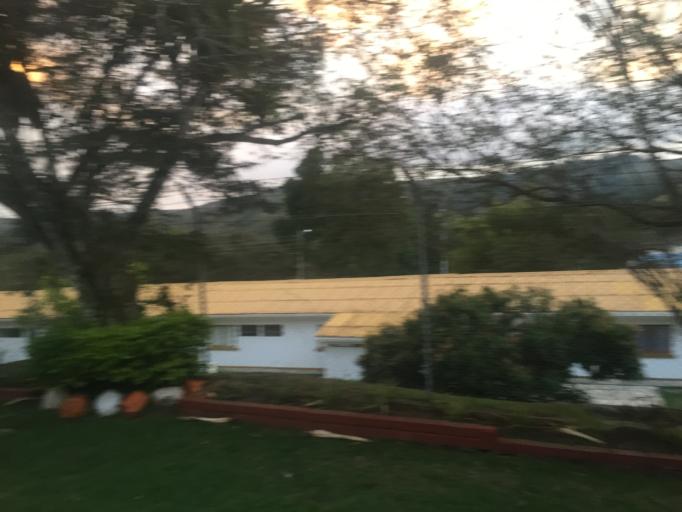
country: CO
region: Valle del Cauca
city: Calimita
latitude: 3.8809
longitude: -76.5381
